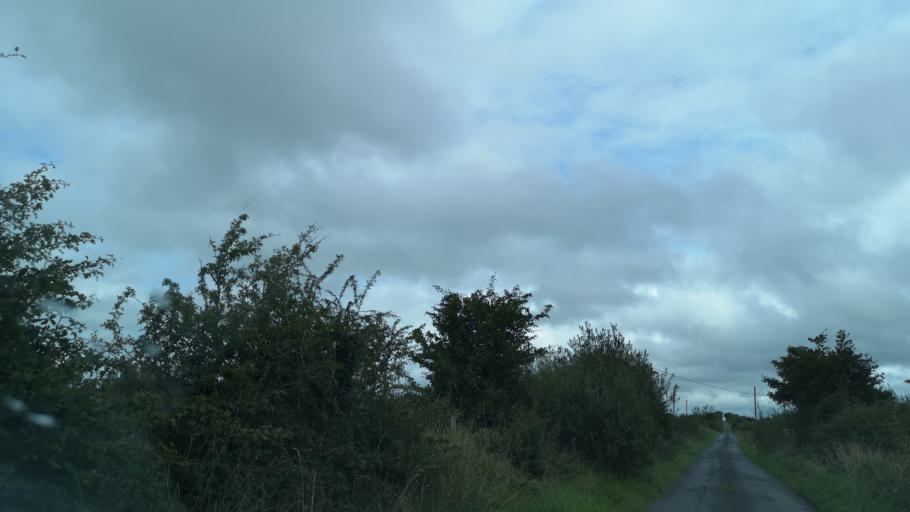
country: IE
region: Connaught
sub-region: County Galway
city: Loughrea
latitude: 53.3025
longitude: -8.5842
